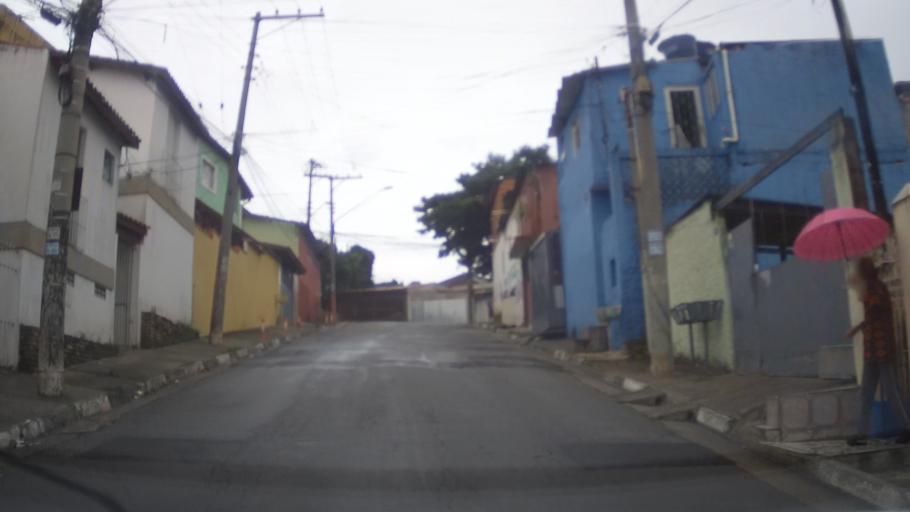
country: BR
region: Sao Paulo
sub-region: Guarulhos
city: Guarulhos
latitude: -23.4725
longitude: -46.5571
